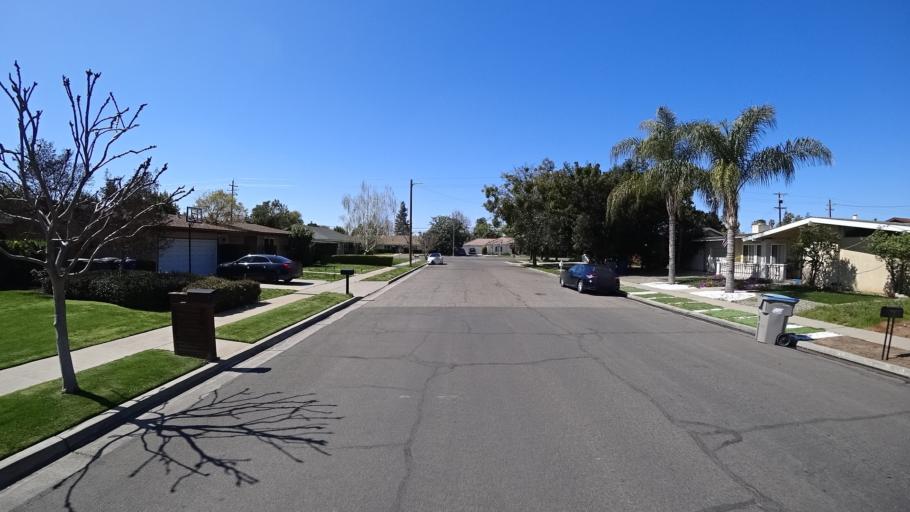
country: US
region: California
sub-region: Fresno County
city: Fresno
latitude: 36.8251
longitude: -119.8071
